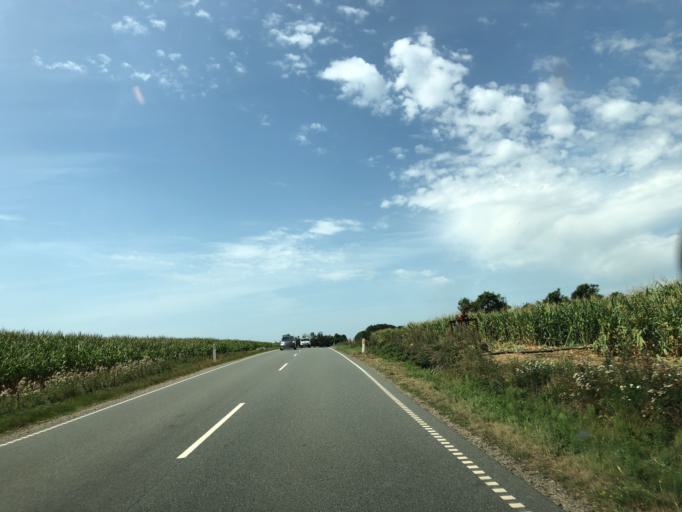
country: DK
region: Central Jutland
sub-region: Ringkobing-Skjern Kommune
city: Skjern
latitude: 56.0274
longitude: 8.4878
